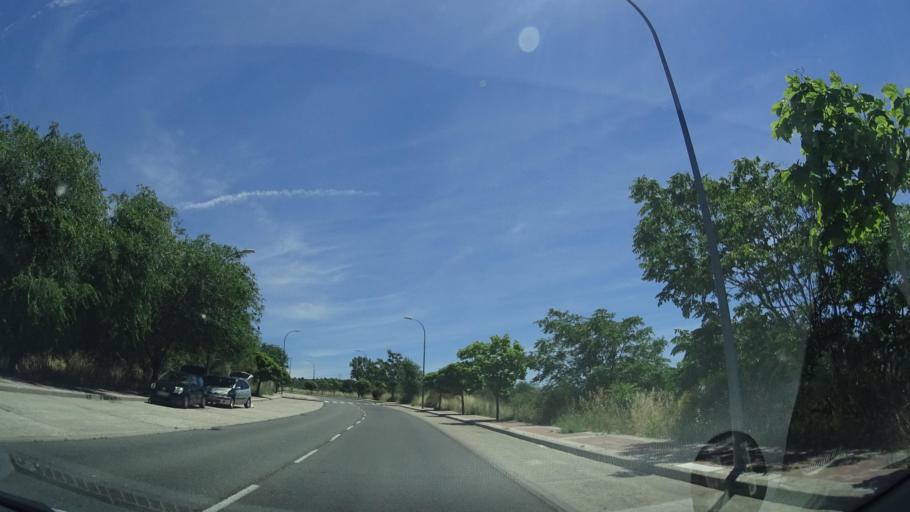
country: ES
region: Madrid
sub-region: Provincia de Madrid
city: Collado-Villalba
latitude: 40.6201
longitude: -3.9903
